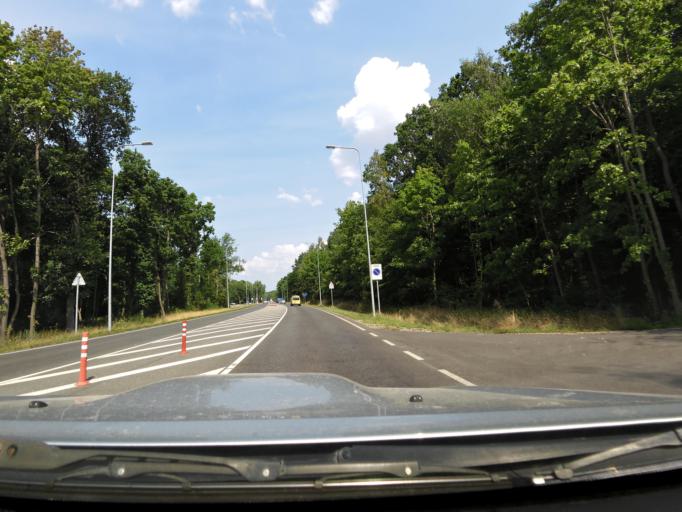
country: LT
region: Klaipedos apskritis
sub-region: Klaipeda
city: Klaipeda
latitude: 55.7598
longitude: 21.0896
